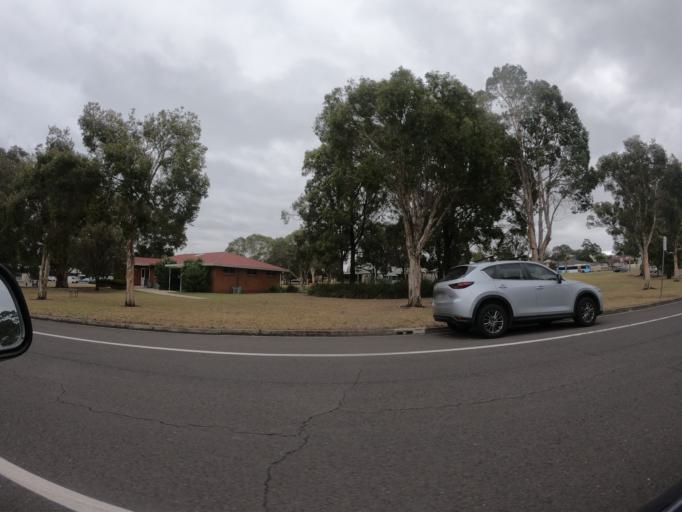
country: AU
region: New South Wales
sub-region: Wollongong
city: Berkeley
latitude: -34.4792
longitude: 150.8479
